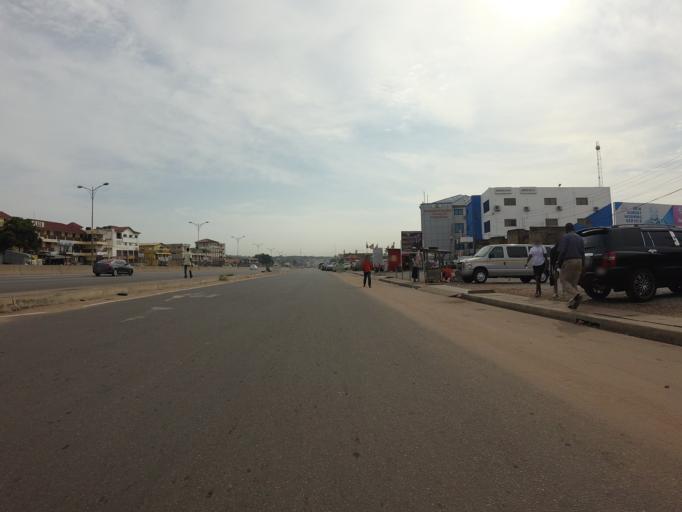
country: GH
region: Greater Accra
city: Dome
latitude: 5.6093
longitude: -0.2371
